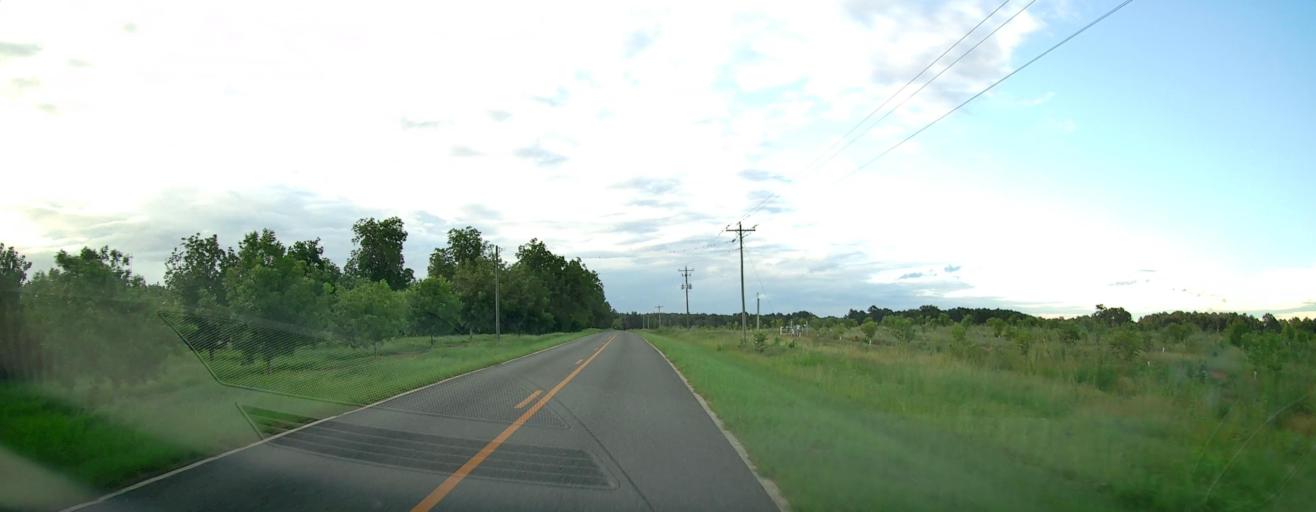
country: US
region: Georgia
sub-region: Pulaski County
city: Hawkinsville
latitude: 32.3167
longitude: -83.5522
